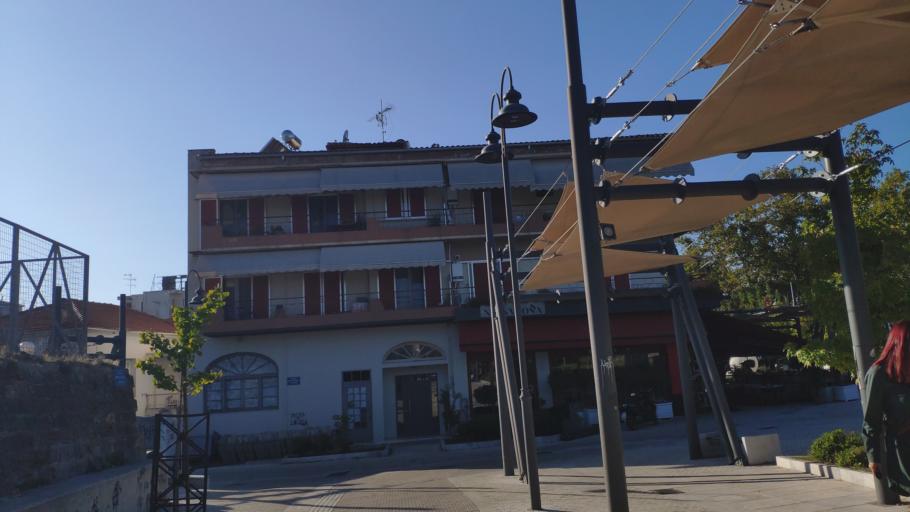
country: GR
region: Thessaly
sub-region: Nomos Larisis
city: Larisa
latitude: 39.6410
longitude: 22.4146
